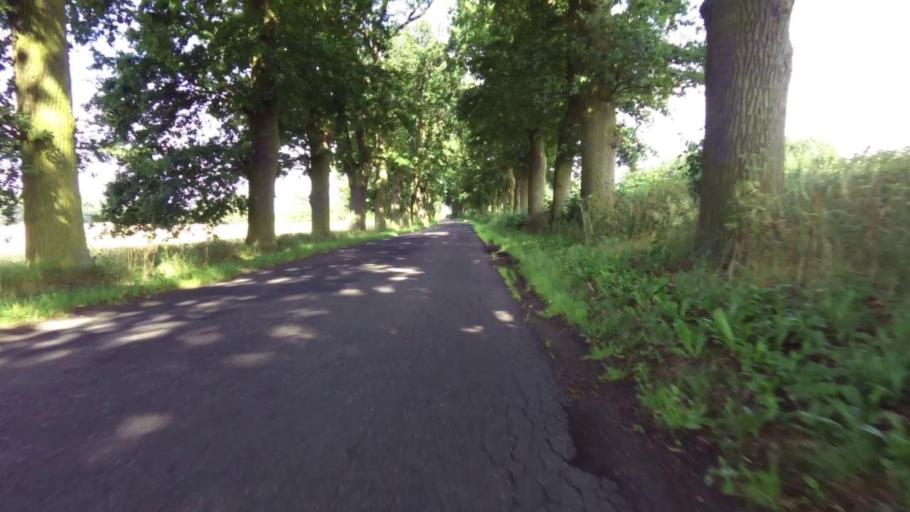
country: PL
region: West Pomeranian Voivodeship
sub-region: Powiat stargardzki
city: Stara Dabrowa
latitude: 53.3429
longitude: 15.1643
